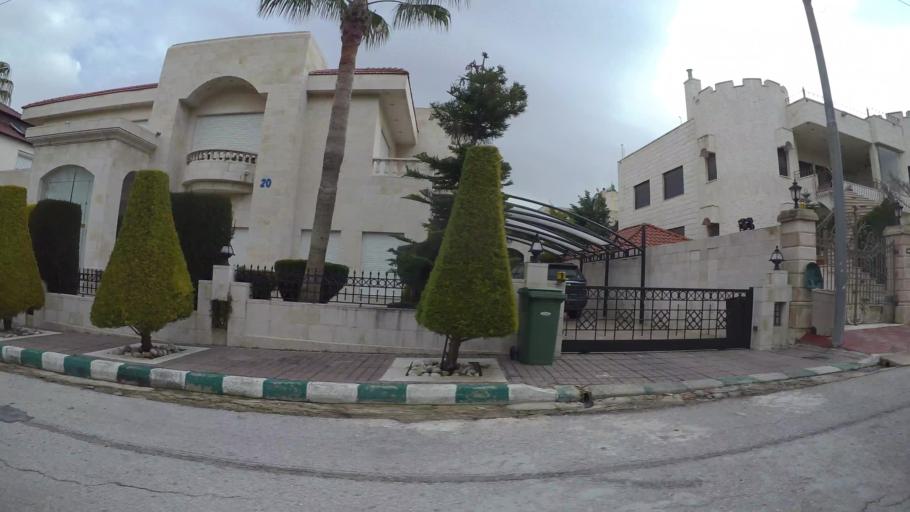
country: JO
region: Amman
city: Wadi as Sir
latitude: 31.9914
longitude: 35.8239
